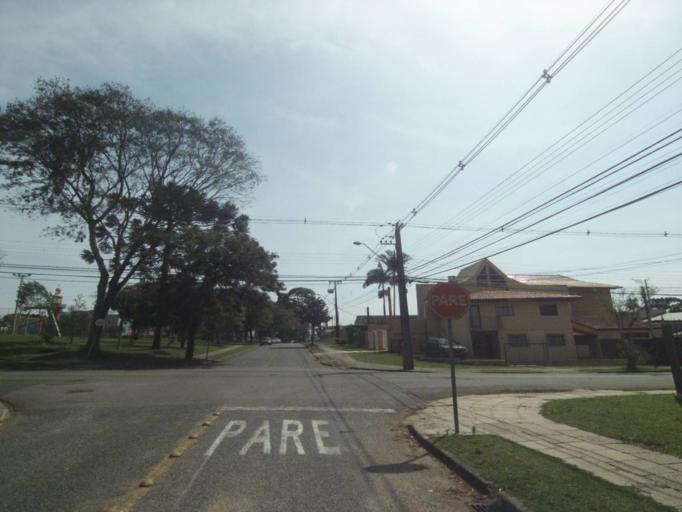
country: BR
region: Parana
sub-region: Curitiba
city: Curitiba
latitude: -25.4616
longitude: -49.3042
